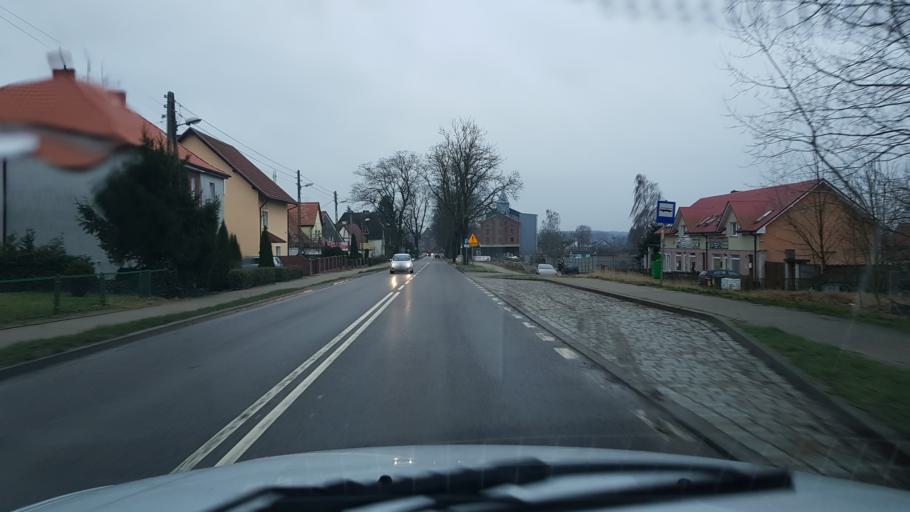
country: PL
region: West Pomeranian Voivodeship
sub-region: Powiat gryficki
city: Ploty
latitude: 53.8122
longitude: 15.2592
